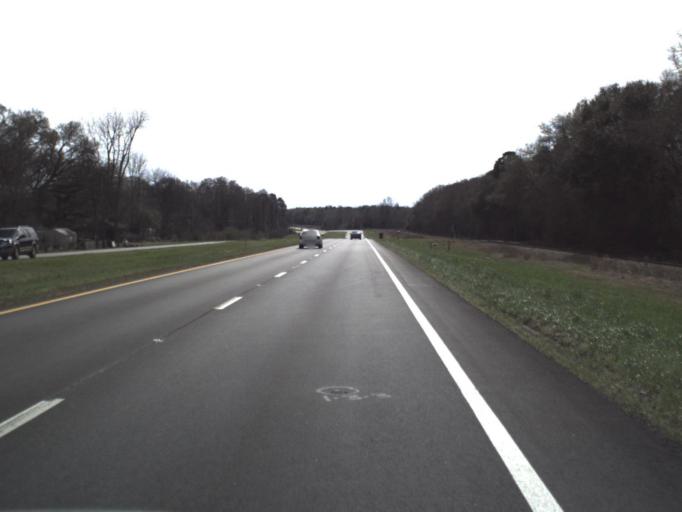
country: US
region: Florida
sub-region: Washington County
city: Chipley
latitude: 30.6802
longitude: -85.3938
